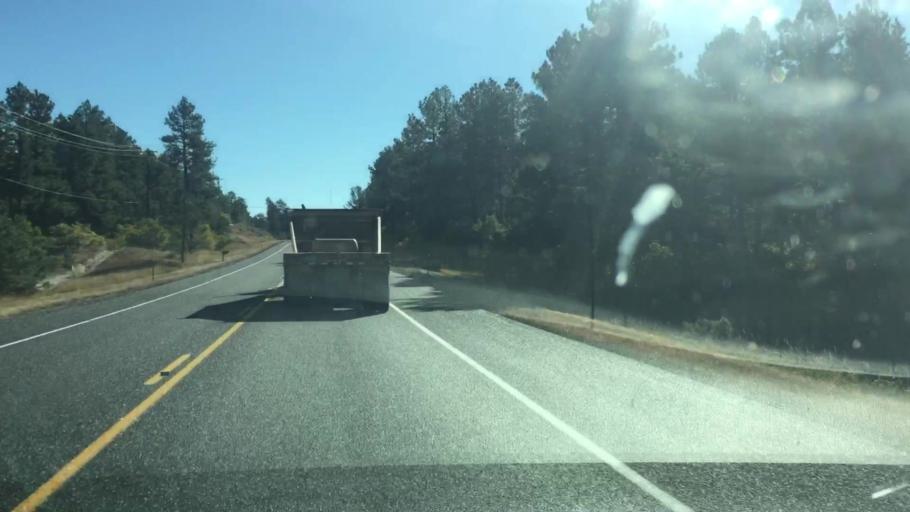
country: US
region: Colorado
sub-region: Elbert County
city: Ponderosa Park
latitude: 39.3787
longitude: -104.7066
